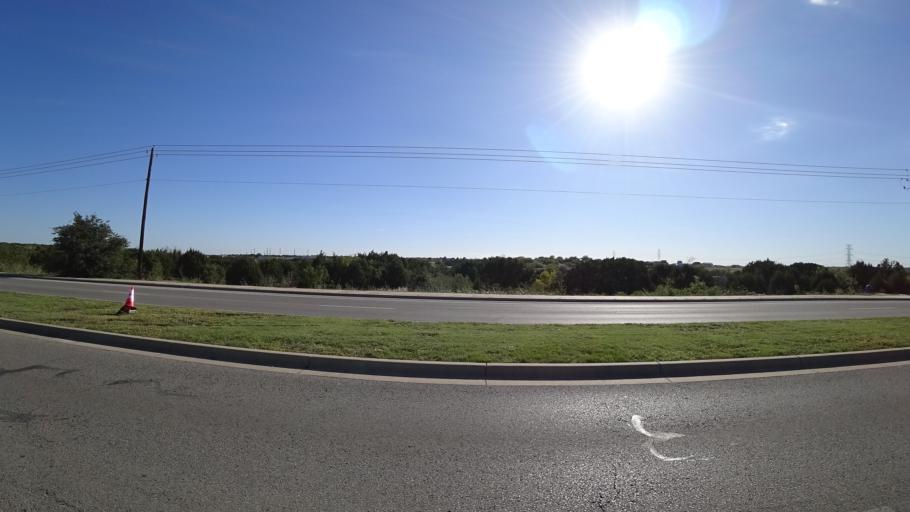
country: US
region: Texas
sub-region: Travis County
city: Hornsby Bend
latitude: 30.2945
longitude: -97.6346
